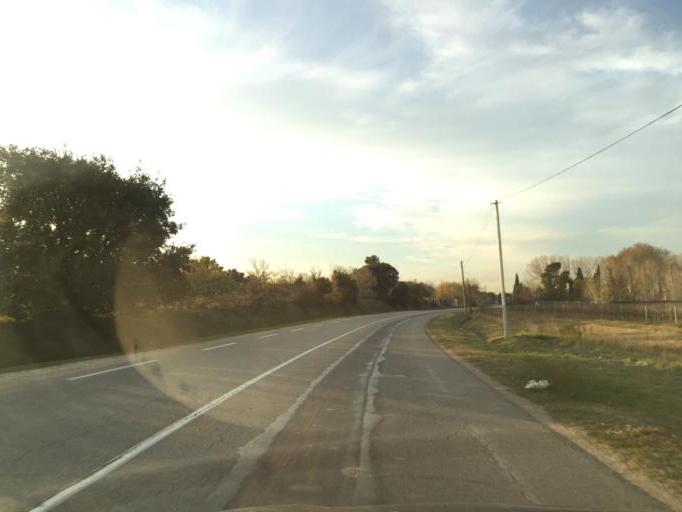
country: FR
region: Provence-Alpes-Cote d'Azur
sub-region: Departement du Vaucluse
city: Courthezon
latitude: 44.1174
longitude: 4.8549
